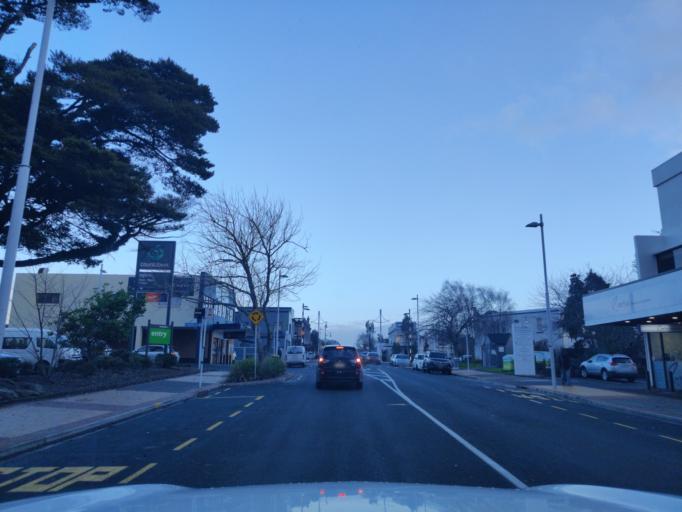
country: NZ
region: Auckland
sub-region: Auckland
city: Pukekohe East
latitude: -37.1995
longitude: 174.9013
